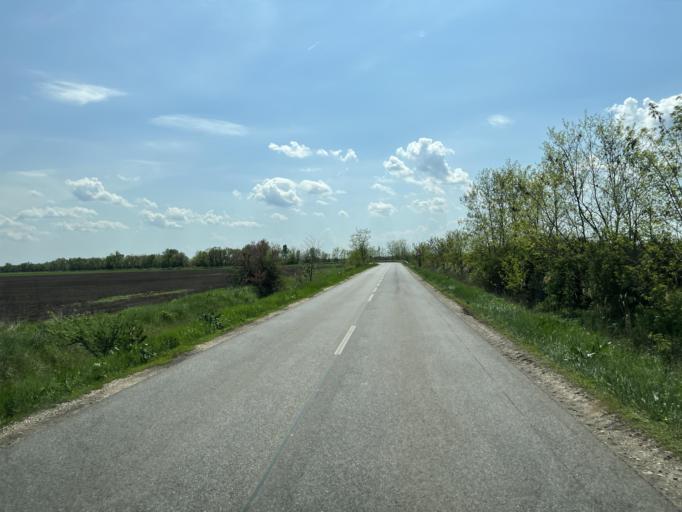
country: HU
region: Pest
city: Cegled
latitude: 47.2274
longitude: 19.7714
